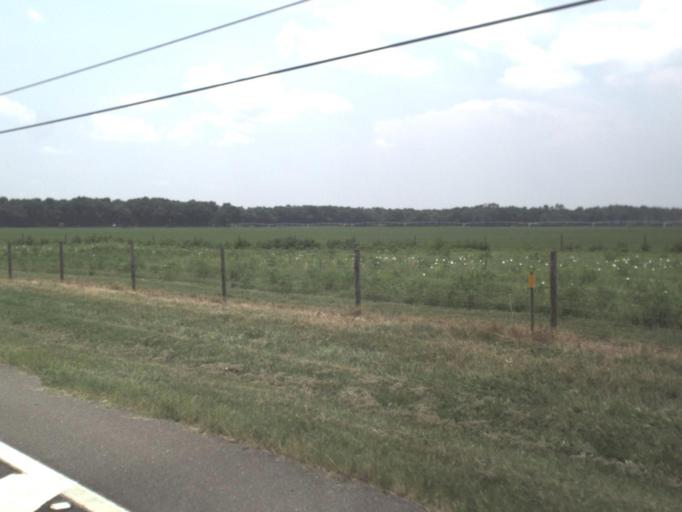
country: US
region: Florida
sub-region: Levy County
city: Manatee Road
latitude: 29.4963
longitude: -82.9463
